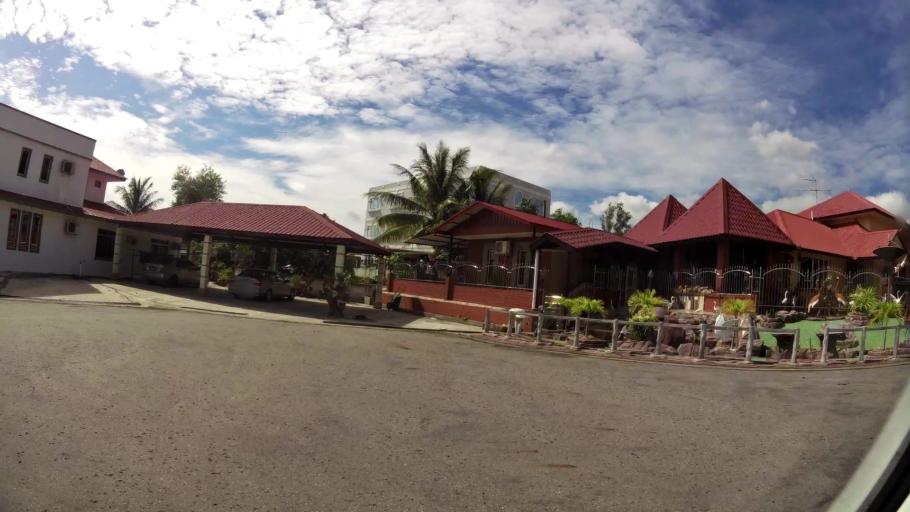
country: BN
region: Brunei and Muara
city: Bandar Seri Begawan
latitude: 4.9313
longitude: 114.9078
